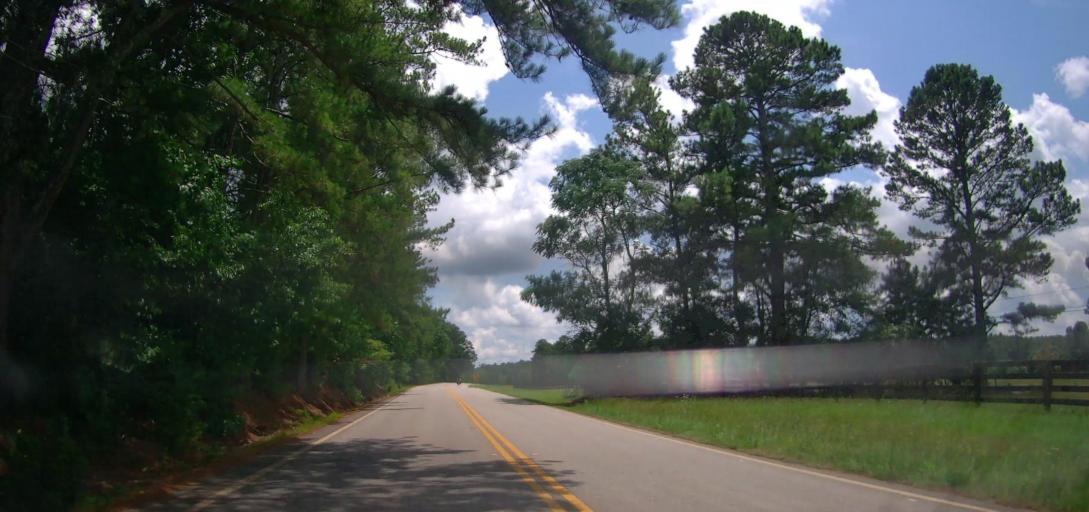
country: US
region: Georgia
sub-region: Troup County
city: Hogansville
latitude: 33.1173
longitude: -84.8099
